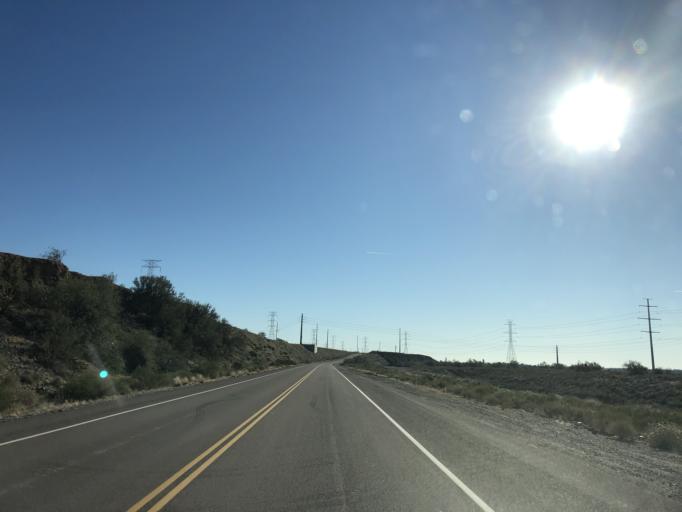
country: US
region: Arizona
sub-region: Maricopa County
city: Sun City West
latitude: 33.6849
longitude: -112.2973
